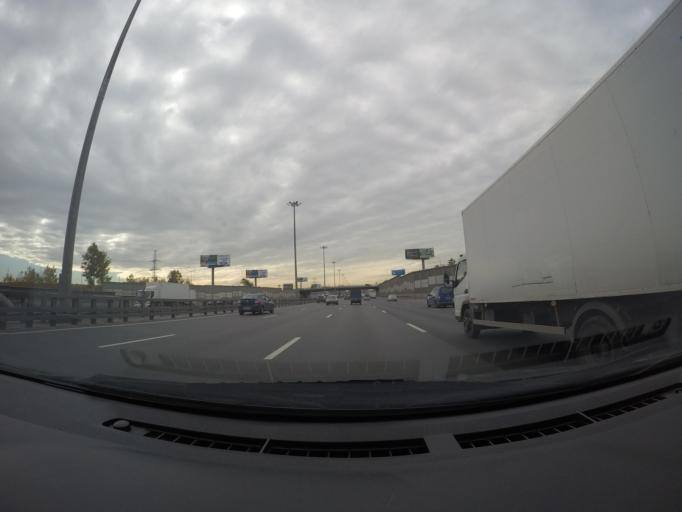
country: RU
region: Moskovskaya
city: Druzhba
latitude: 55.8975
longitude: 37.7514
